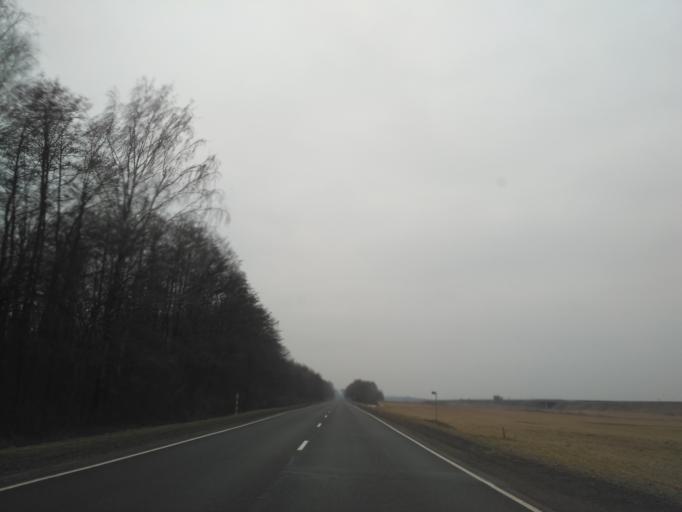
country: BY
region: Brest
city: Baranovichi
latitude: 53.2172
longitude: 26.1505
